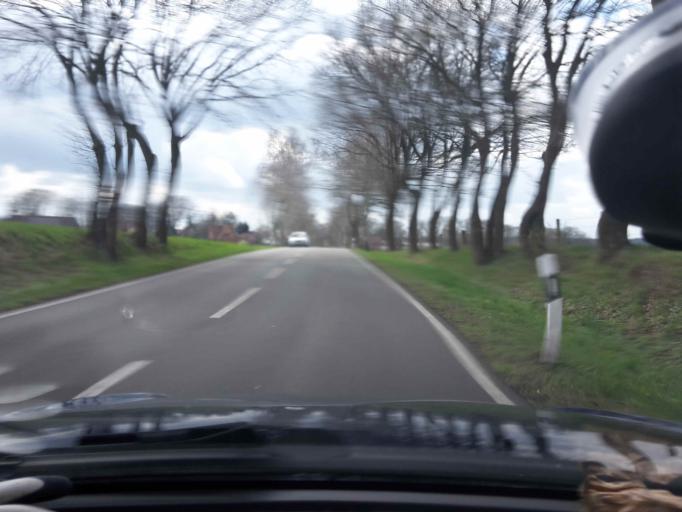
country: DE
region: Lower Saxony
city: Hanstedt
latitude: 53.2409
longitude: 10.0279
